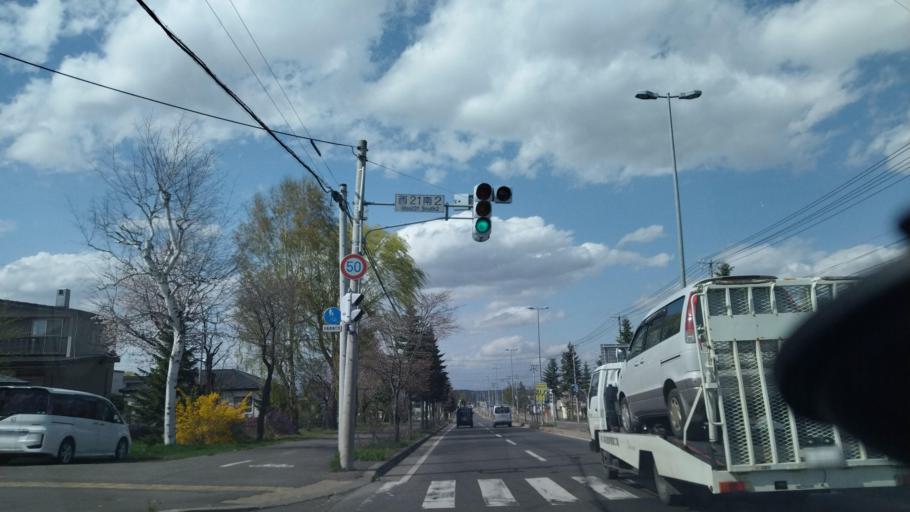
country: JP
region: Hokkaido
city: Obihiro
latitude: 42.9201
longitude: 143.1441
